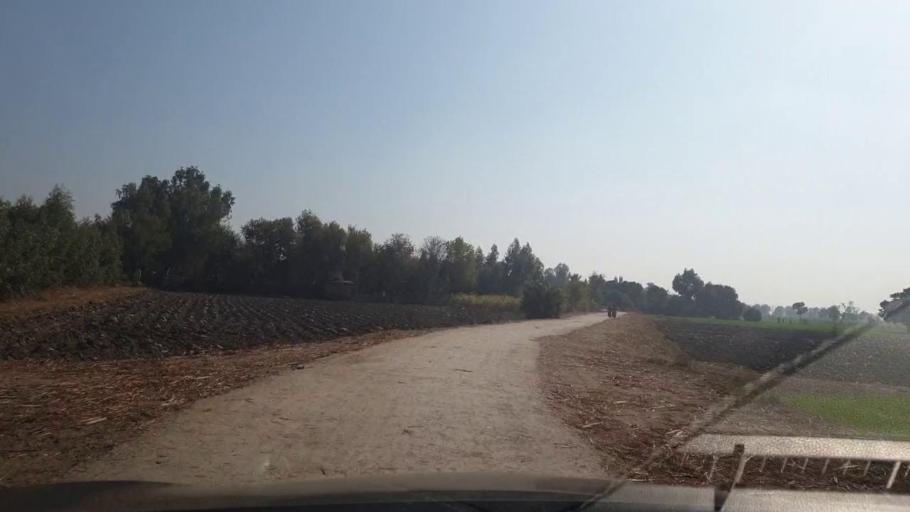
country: PK
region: Sindh
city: Ubauro
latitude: 28.1469
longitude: 69.6918
